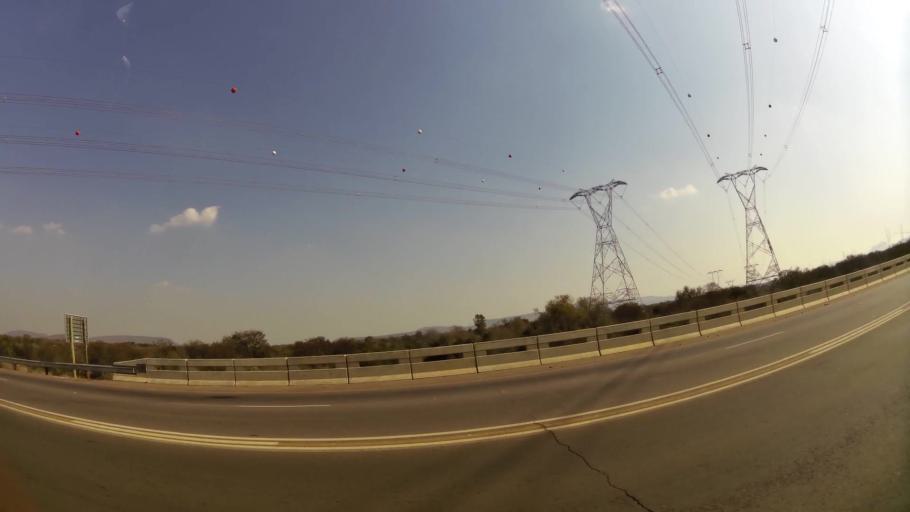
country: ZA
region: North-West
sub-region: Bojanala Platinum District Municipality
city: Mogwase
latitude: -25.3933
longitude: 27.0710
